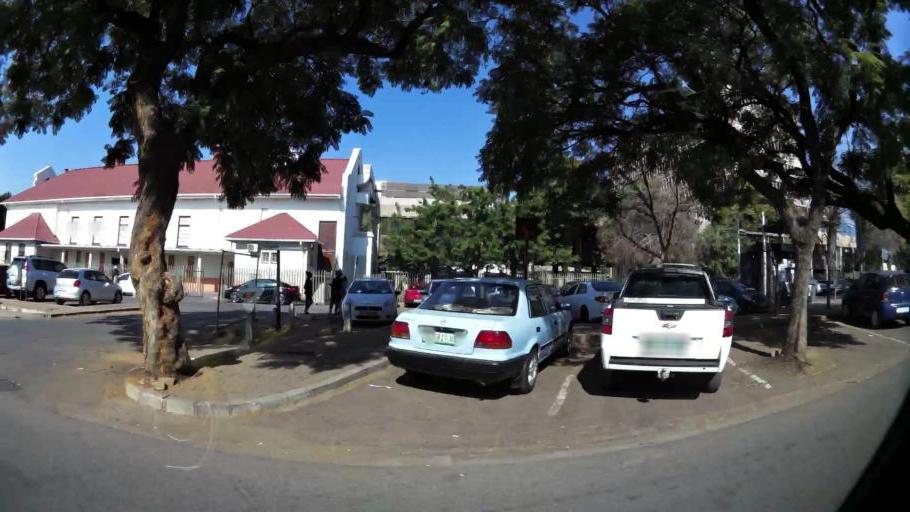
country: ZA
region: North-West
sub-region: Bojanala Platinum District Municipality
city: Rustenburg
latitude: -25.6720
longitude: 27.2441
